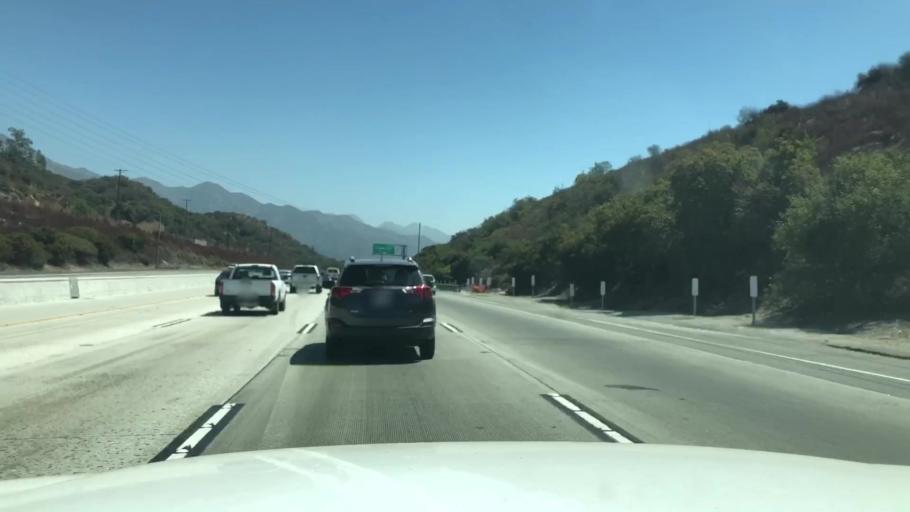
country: US
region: California
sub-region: Los Angeles County
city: La Crescenta-Montrose
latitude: 34.2342
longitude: -118.2844
